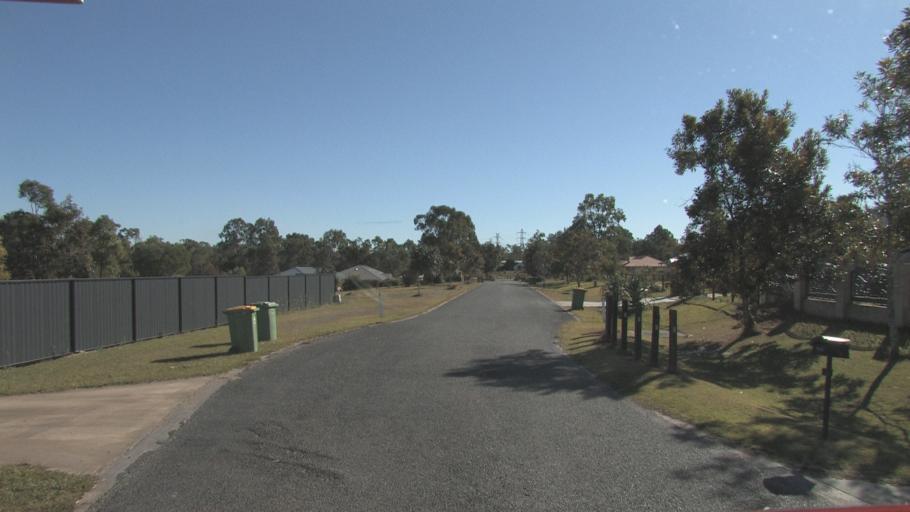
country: AU
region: Queensland
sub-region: Logan
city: North Maclean
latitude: -27.7385
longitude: 152.9556
